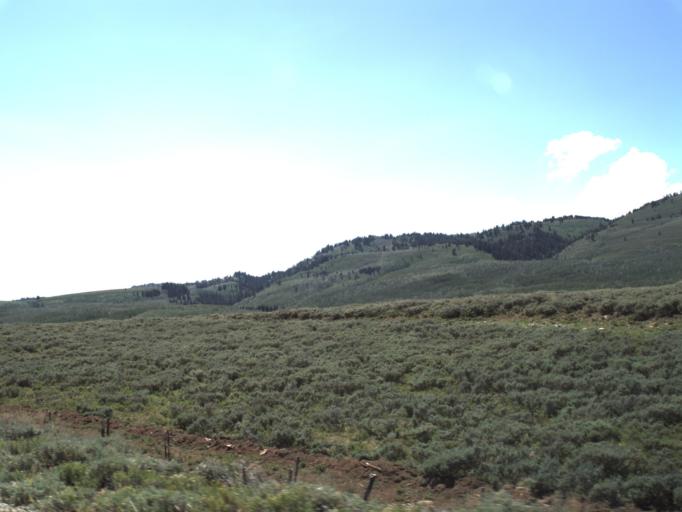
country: US
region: Utah
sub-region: Rich County
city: Randolph
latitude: 41.4837
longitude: -111.4263
